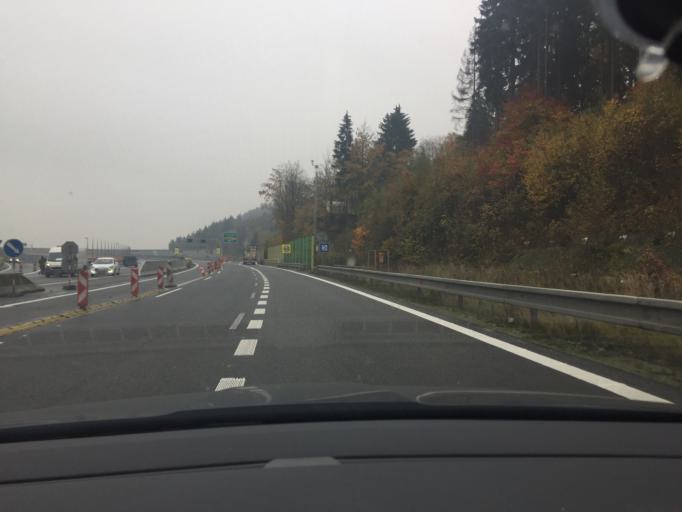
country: SK
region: Zilinsky
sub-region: Okres Zilina
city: Zilina
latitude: 49.2435
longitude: 18.6886
